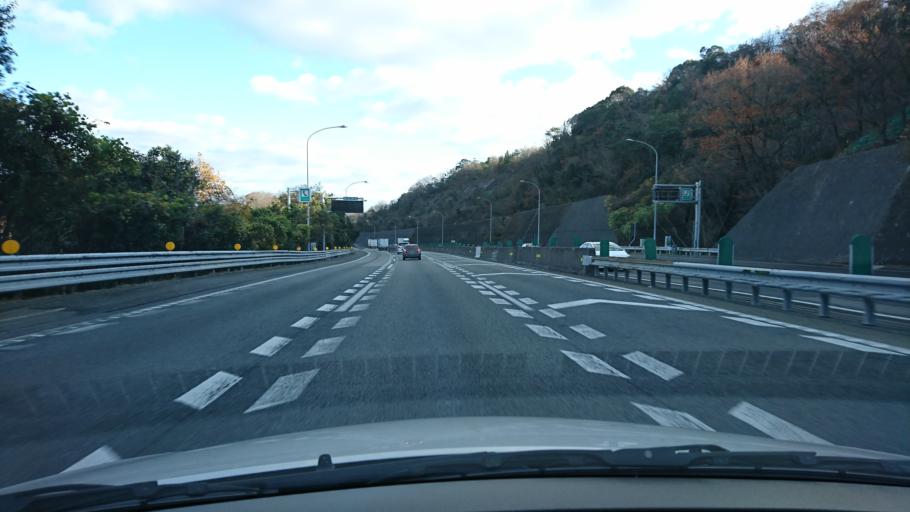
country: JP
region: Hyogo
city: Takarazuka
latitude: 34.8263
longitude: 135.3056
